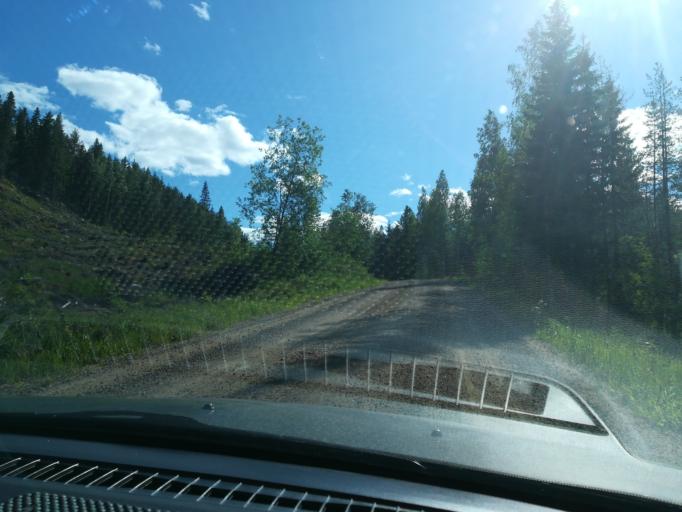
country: FI
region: Southern Savonia
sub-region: Mikkeli
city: Puumala
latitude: 61.6548
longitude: 28.1116
